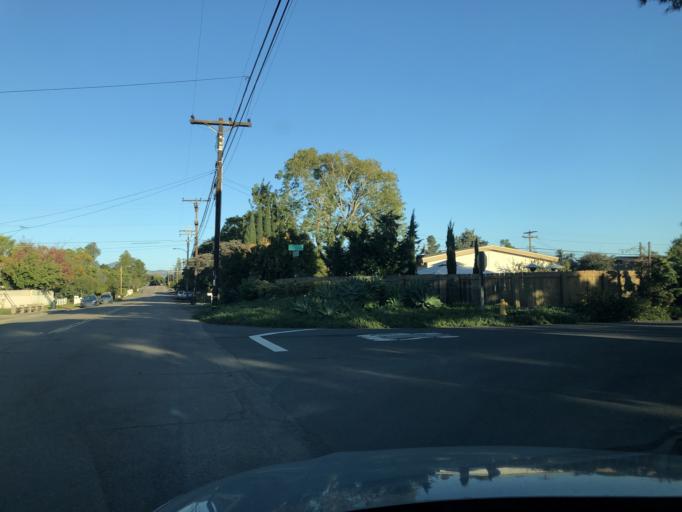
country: US
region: California
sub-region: San Diego County
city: Bonita
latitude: 32.6550
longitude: -117.0587
